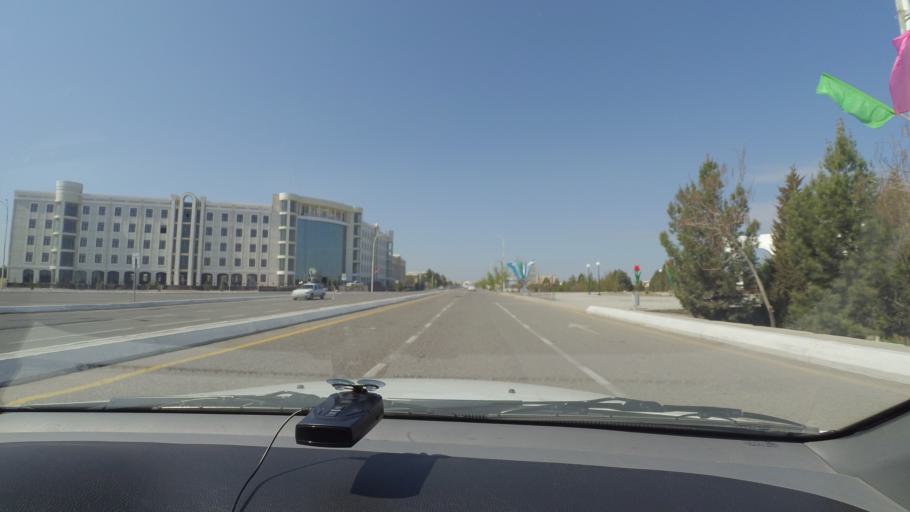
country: UZ
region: Bukhara
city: Bukhara
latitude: 39.7672
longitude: 64.4722
